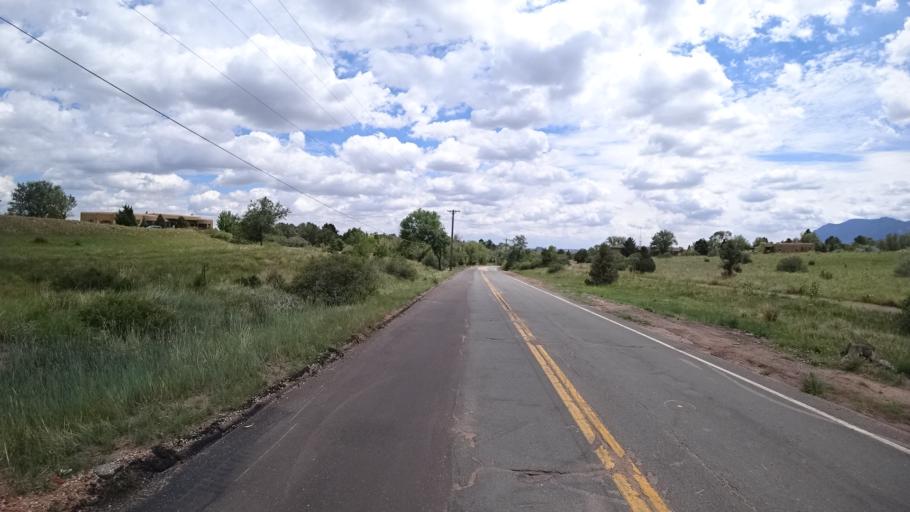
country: US
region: Colorado
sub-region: El Paso County
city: Colorado Springs
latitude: 38.8549
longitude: -104.8440
